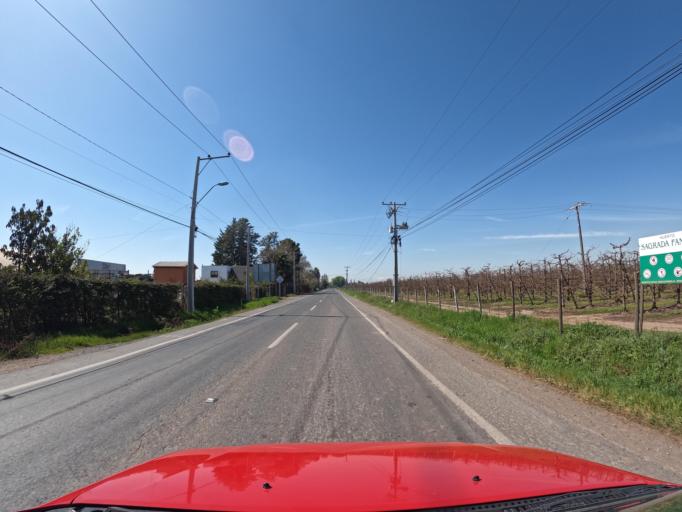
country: CL
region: Maule
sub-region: Provincia de Curico
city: Rauco
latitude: -34.9958
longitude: -71.3597
